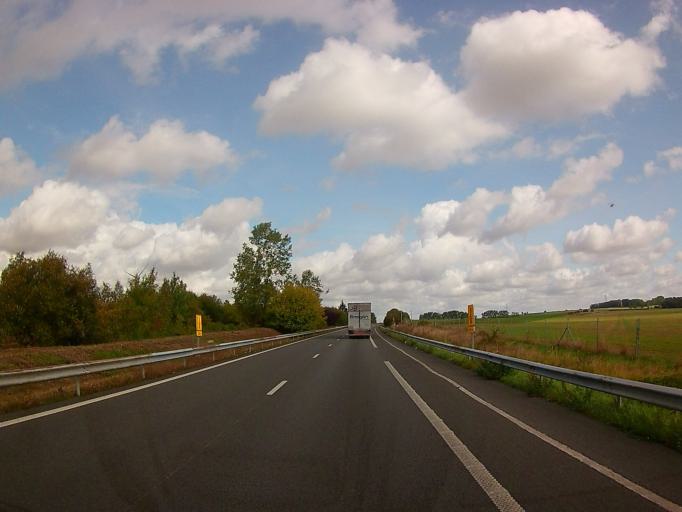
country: FR
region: Picardie
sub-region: Departement de la Somme
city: Moislains
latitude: 50.0231
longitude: 2.8863
